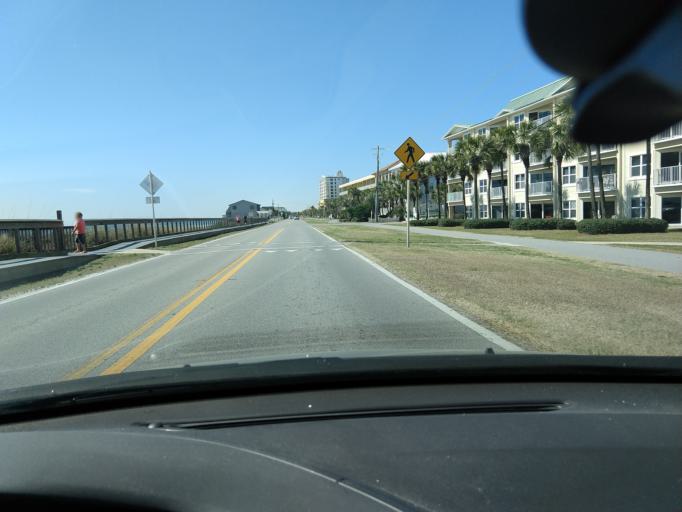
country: US
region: Florida
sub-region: Walton County
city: Miramar Beach
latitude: 30.3788
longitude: -86.3914
